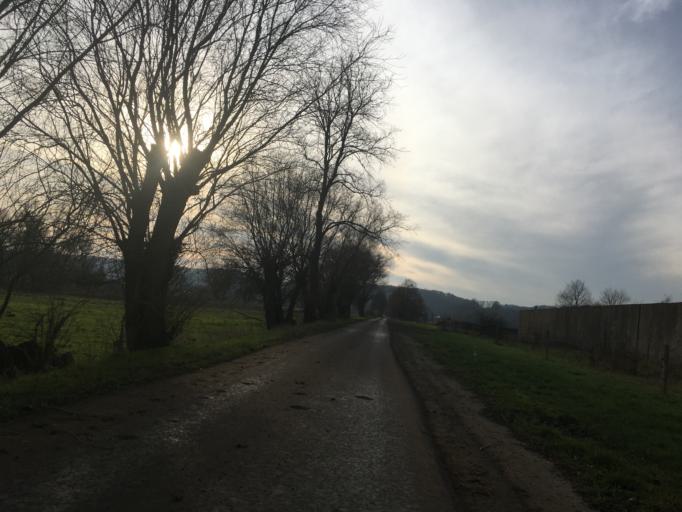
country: DE
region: Brandenburg
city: Falkenberg
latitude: 52.8134
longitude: 13.9692
